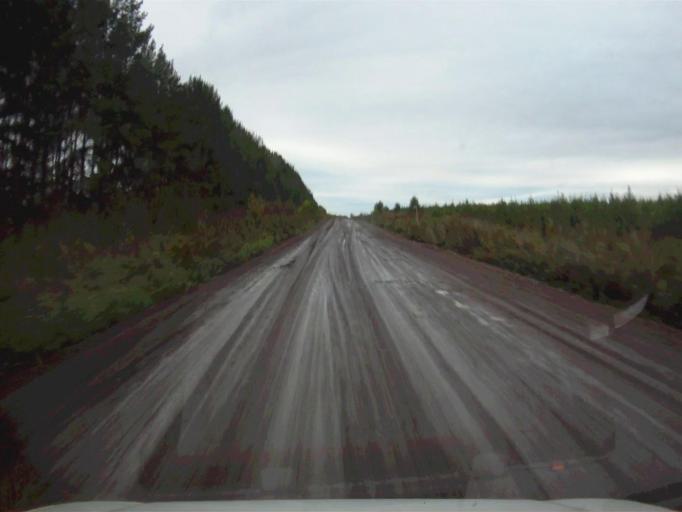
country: RU
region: Chelyabinsk
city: Nyazepetrovsk
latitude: 56.1447
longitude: 59.2840
